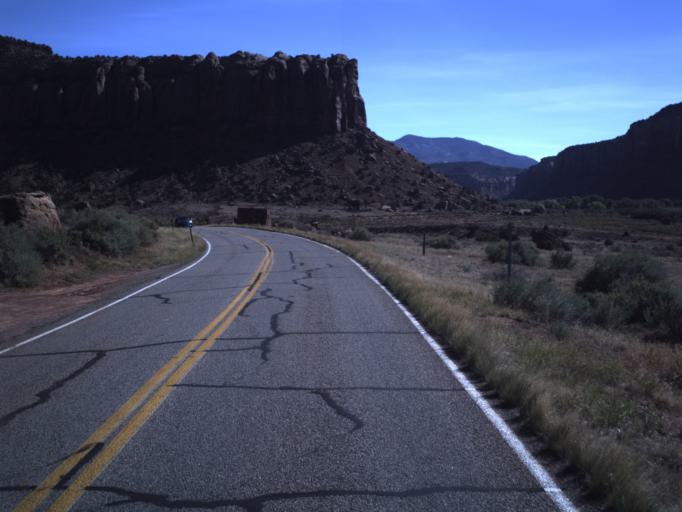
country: US
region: Utah
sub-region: San Juan County
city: Monticello
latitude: 38.0622
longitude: -109.5517
